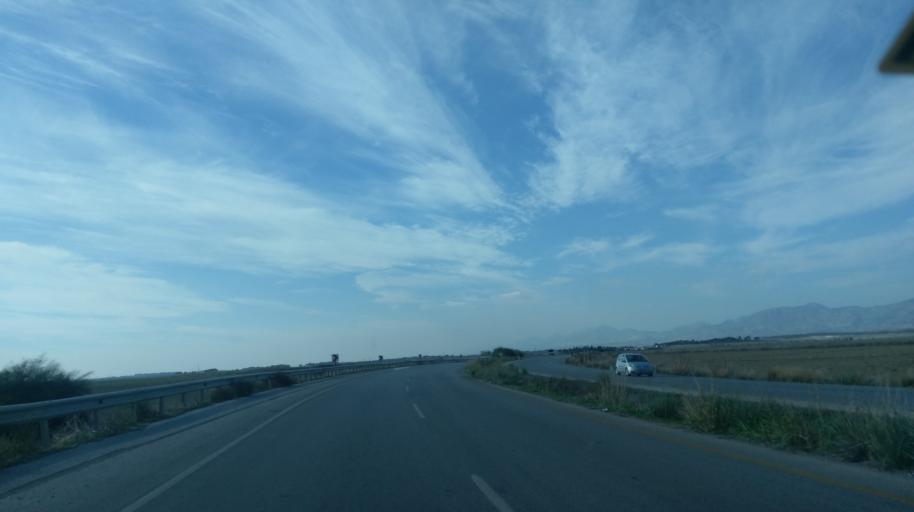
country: CY
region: Ammochostos
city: Lefkonoiko
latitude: 35.1879
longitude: 33.6333
